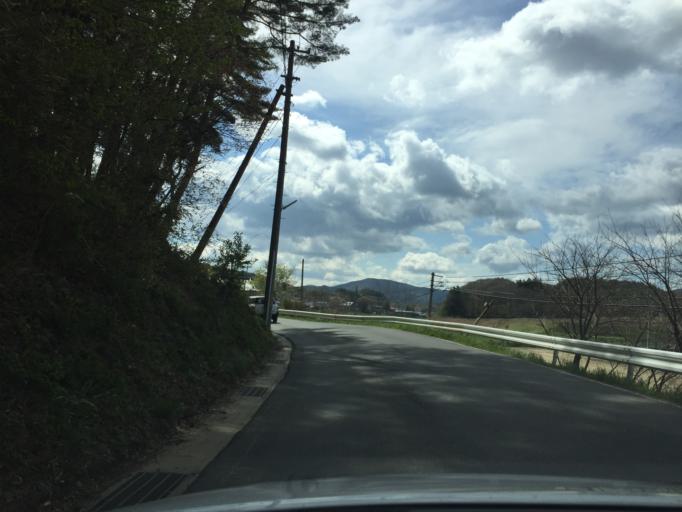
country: JP
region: Fukushima
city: Funehikimachi-funehiki
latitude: 37.6078
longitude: 140.6663
